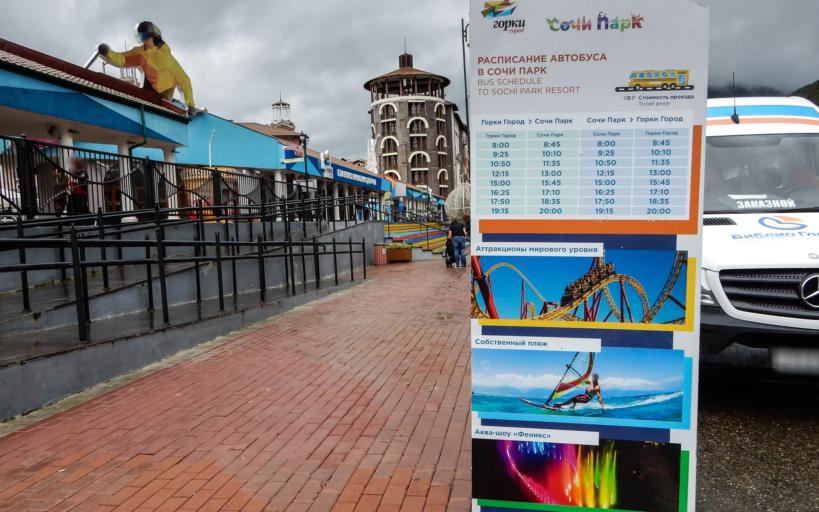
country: RU
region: Krasnodarskiy
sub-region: Sochi City
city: Krasnaya Polyana
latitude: 43.6833
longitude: 40.2677
